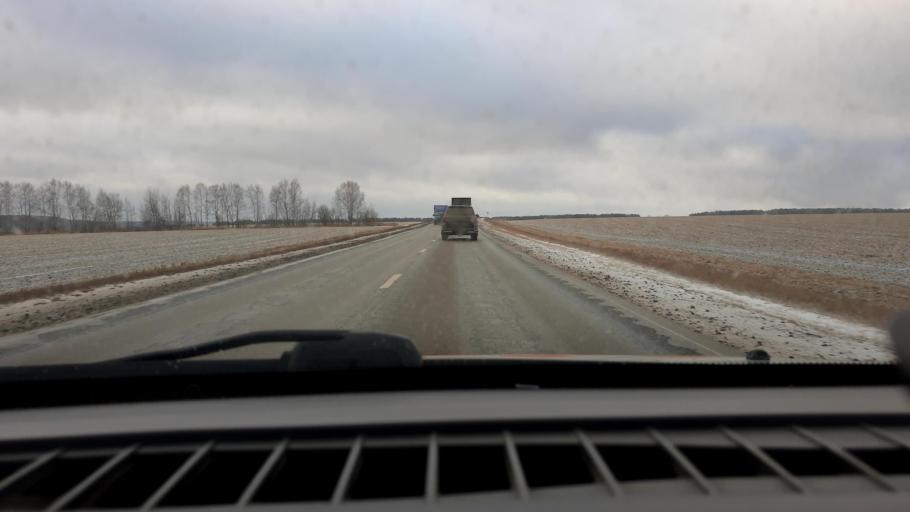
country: RU
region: Nizjnij Novgorod
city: Bogorodsk
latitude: 56.0934
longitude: 43.5772
